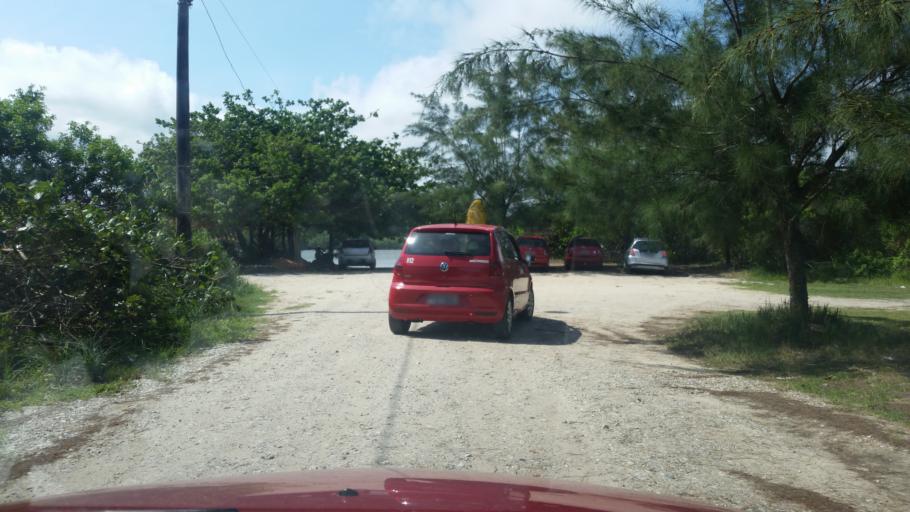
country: BR
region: Sao Paulo
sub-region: Iguape
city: Iguape
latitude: -24.6935
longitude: -47.4529
